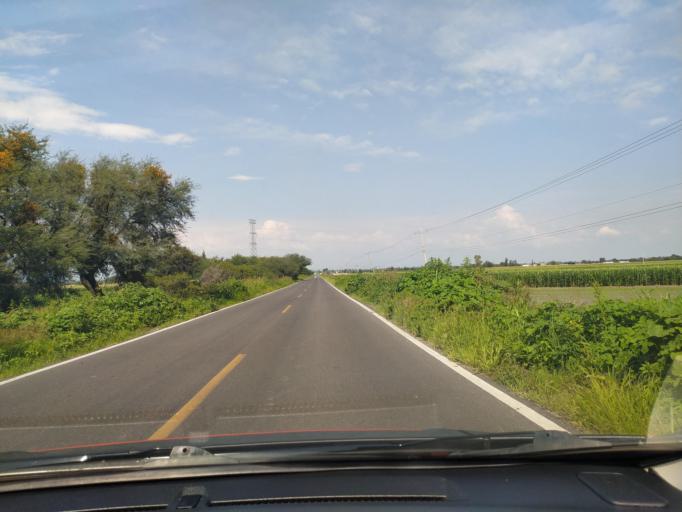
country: MX
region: Guanajuato
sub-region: San Francisco del Rincon
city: Fraccionamiento la Mezquitera
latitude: 20.9921
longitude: -101.8227
